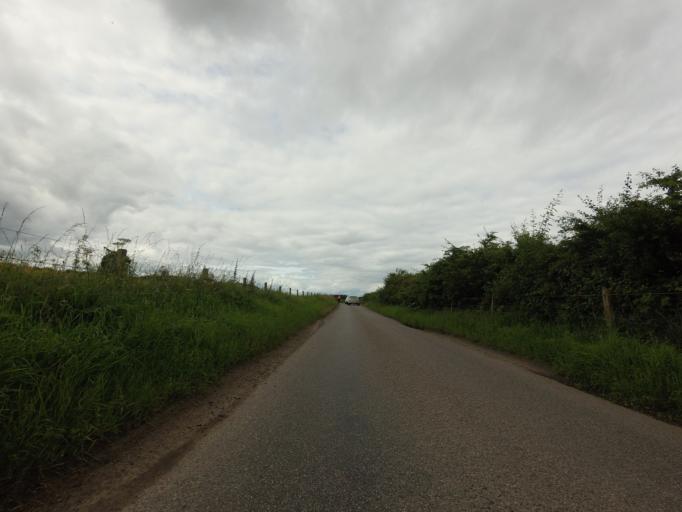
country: GB
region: Scotland
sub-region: Moray
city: Forres
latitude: 57.6227
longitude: -3.6705
